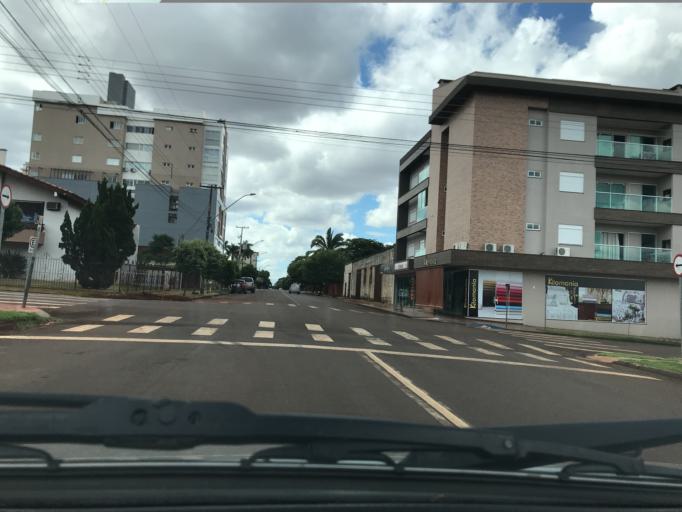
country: BR
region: Parana
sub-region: Palotina
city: Palotina
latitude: -24.2874
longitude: -53.8374
